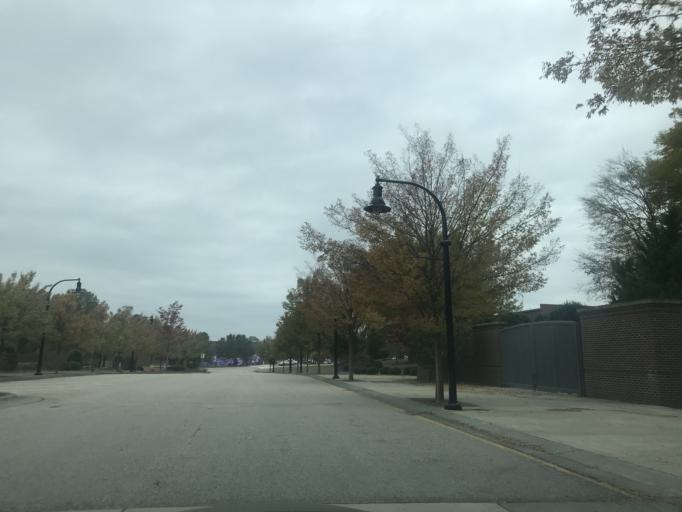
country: US
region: North Carolina
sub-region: Wake County
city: Wake Forest
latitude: 35.9763
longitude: -78.5079
